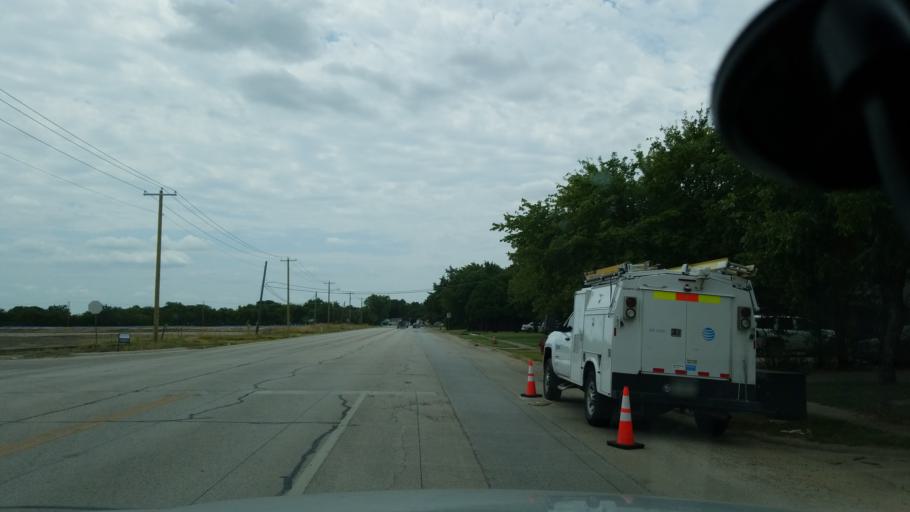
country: US
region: Texas
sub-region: Dallas County
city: Grand Prairie
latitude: 32.7412
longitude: -96.9878
